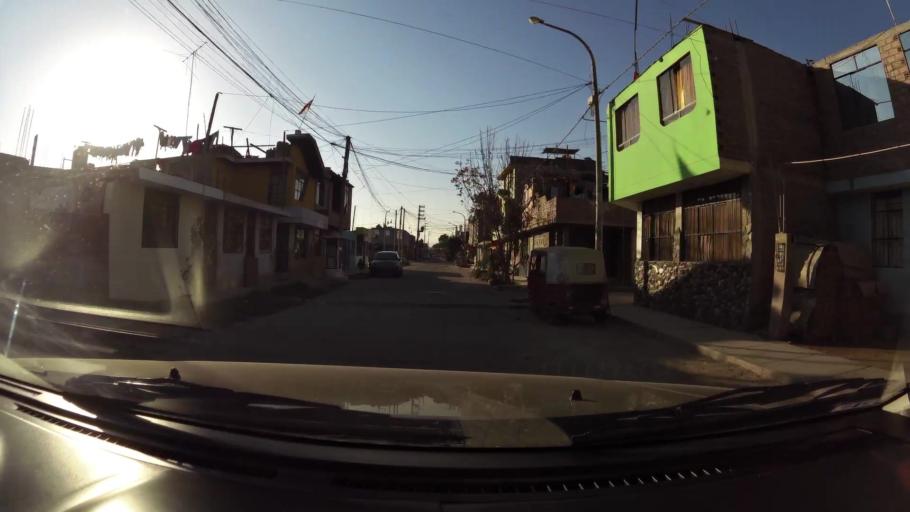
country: PE
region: Ica
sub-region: Provincia de Ica
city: Ica
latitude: -14.0666
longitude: -75.7204
